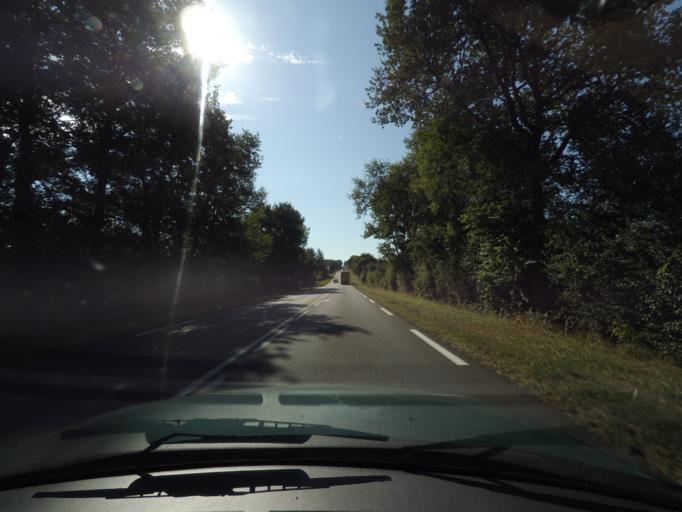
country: FR
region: Poitou-Charentes
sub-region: Departement de la Vienne
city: Terce
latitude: 46.4481
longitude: 0.5727
